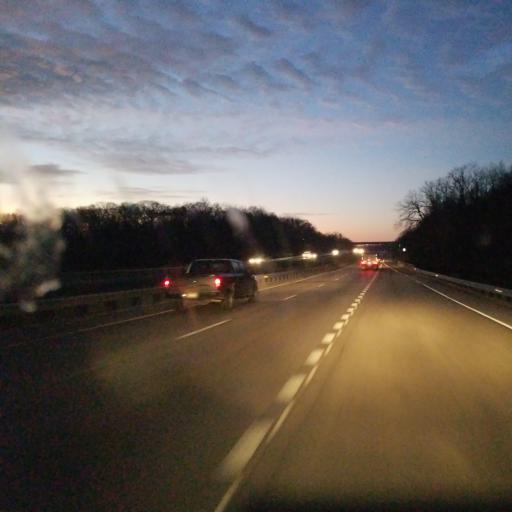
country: US
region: Illinois
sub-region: Peoria County
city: Bellevue
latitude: 40.6894
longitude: -89.6758
